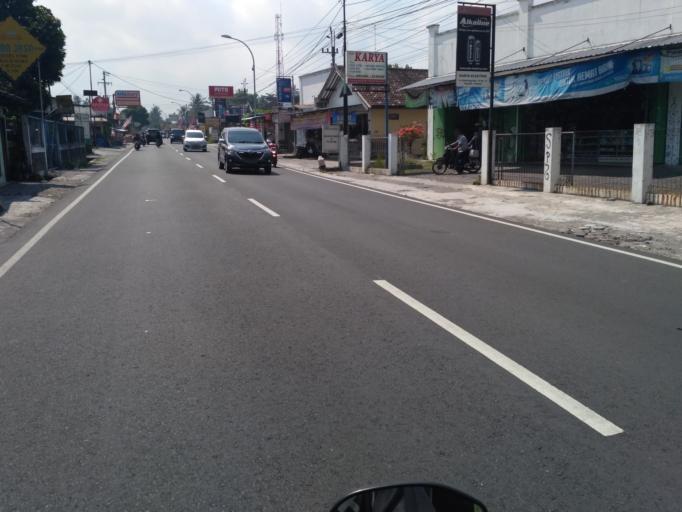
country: ID
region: Daerah Istimewa Yogyakarta
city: Melati
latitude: -7.7058
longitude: 110.4119
